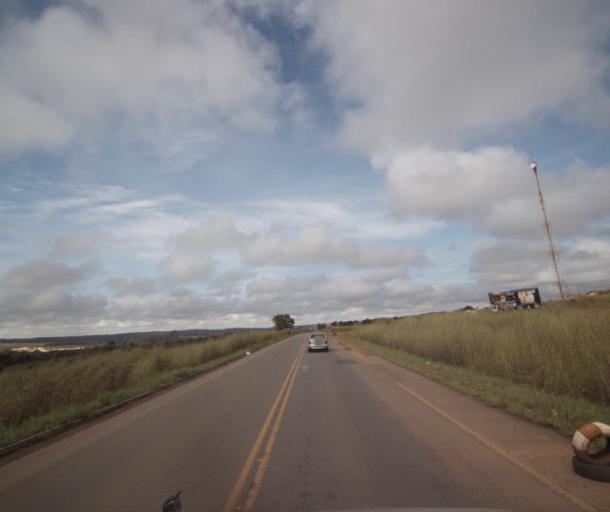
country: BR
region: Goias
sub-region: Pirenopolis
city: Pirenopolis
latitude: -15.7666
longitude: -48.7593
